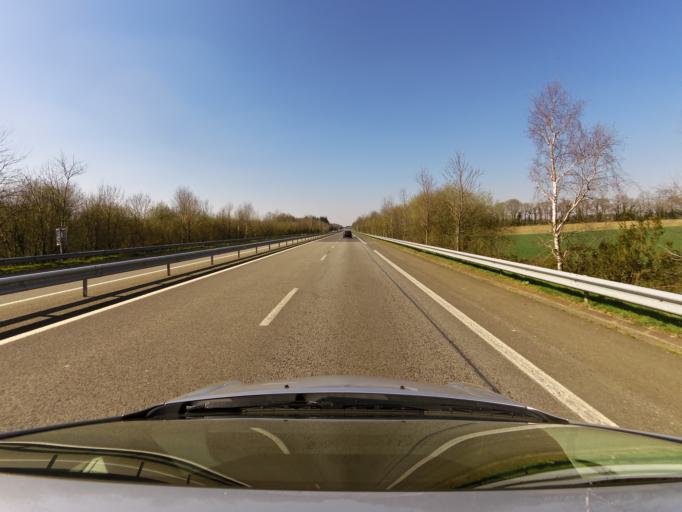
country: FR
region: Brittany
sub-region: Departement du Morbihan
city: Campeneac
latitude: 47.9300
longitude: -2.3248
